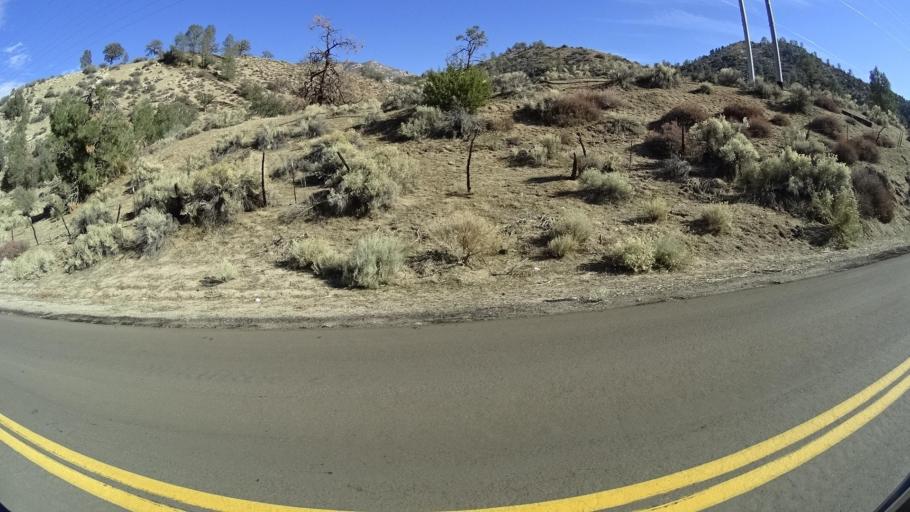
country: US
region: California
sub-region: Kern County
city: Bodfish
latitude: 35.5303
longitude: -118.5122
